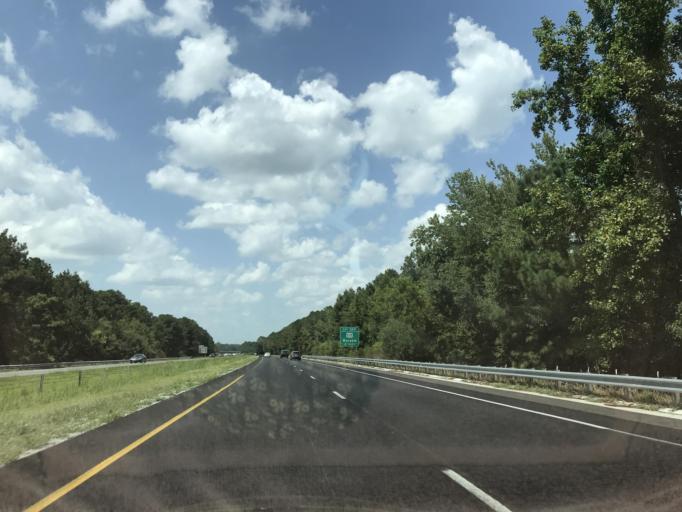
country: US
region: North Carolina
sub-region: Duplin County
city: Kenansville
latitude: 34.9289
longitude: -78.0378
